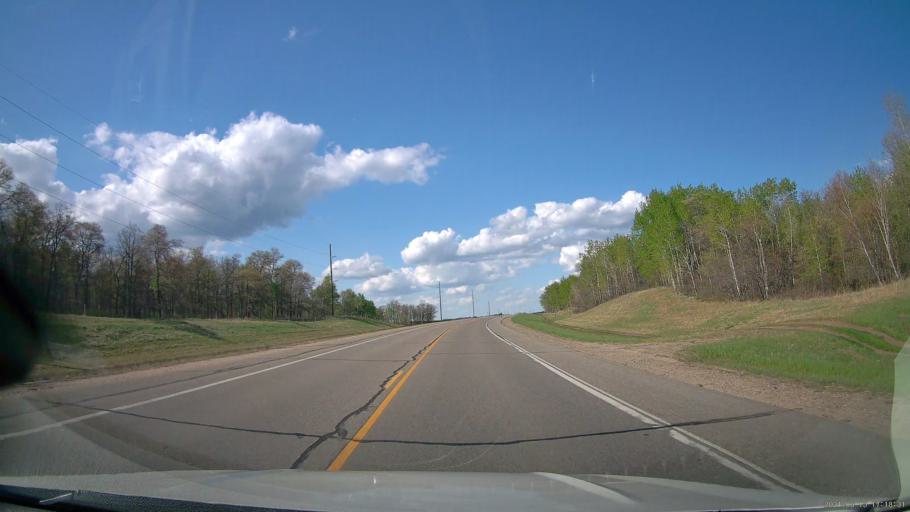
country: US
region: Minnesota
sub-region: Hubbard County
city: Park Rapids
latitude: 46.9628
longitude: -95.0182
